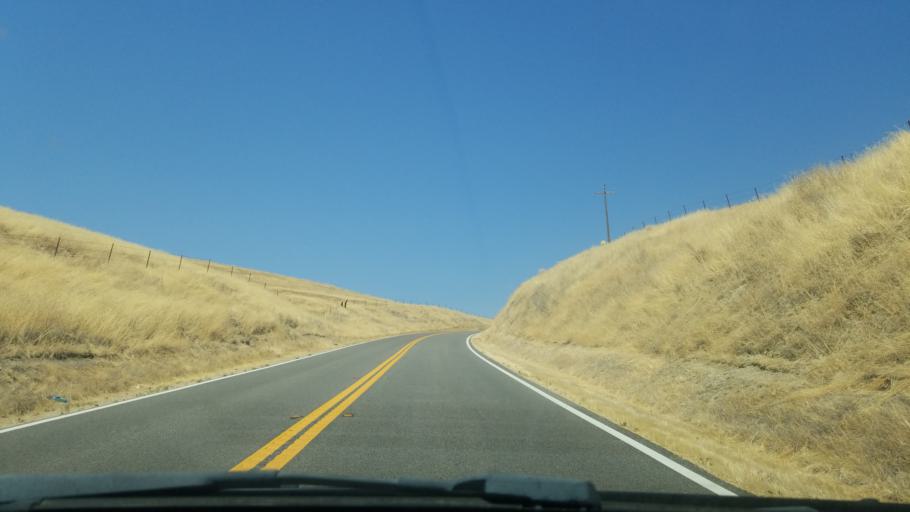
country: US
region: California
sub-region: San Luis Obispo County
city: Shandon
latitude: 35.5907
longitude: -120.4212
